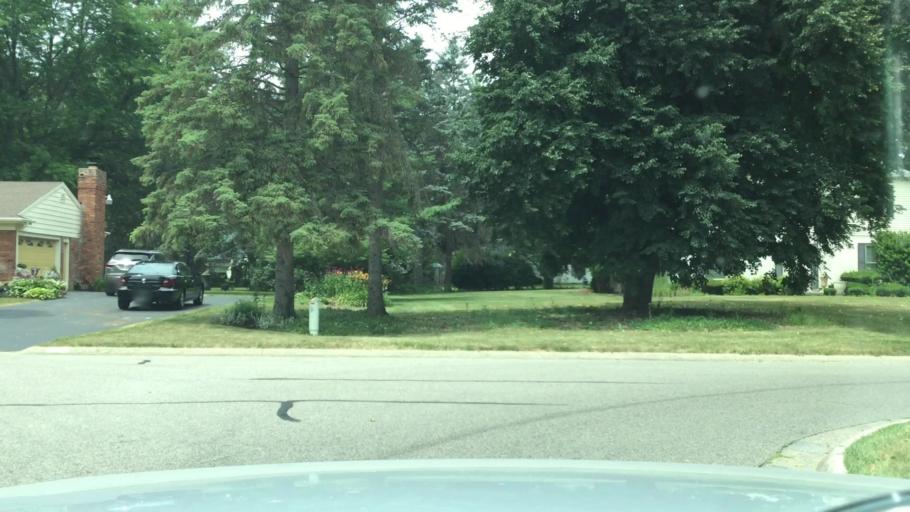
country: US
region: Michigan
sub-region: Genesee County
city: Swartz Creek
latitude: 43.0180
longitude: -83.7947
